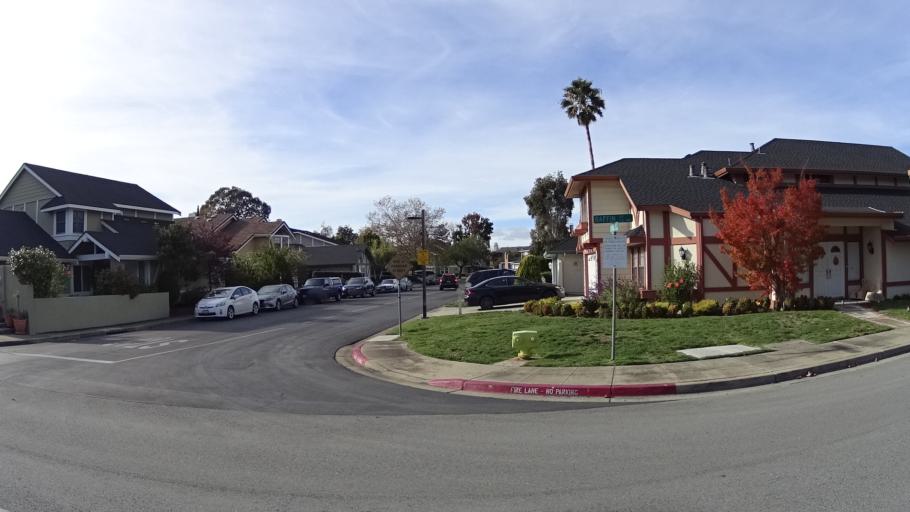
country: US
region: California
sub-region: San Mateo County
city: Redwood Shores
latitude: 37.5404
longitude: -122.2608
